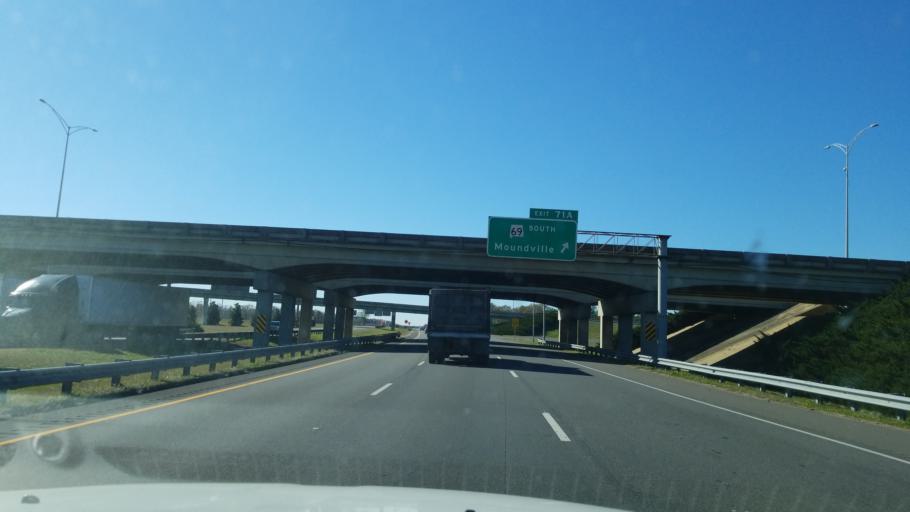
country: US
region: Alabama
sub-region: Tuscaloosa County
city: Tuscaloosa
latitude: 33.1705
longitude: -87.5522
